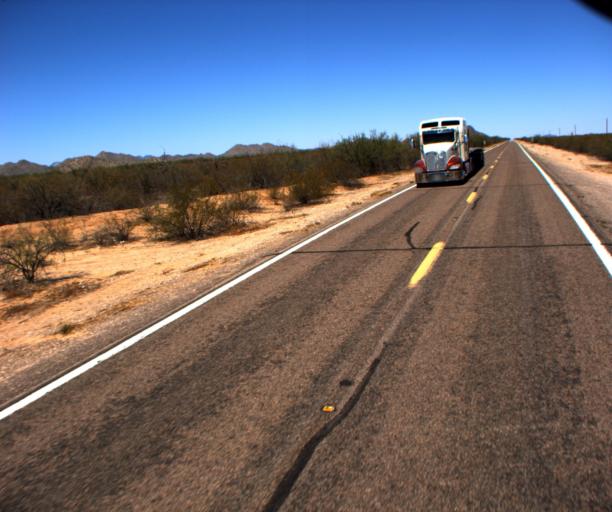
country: US
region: Arizona
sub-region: Pima County
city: Ajo
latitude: 32.1984
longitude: -112.4795
